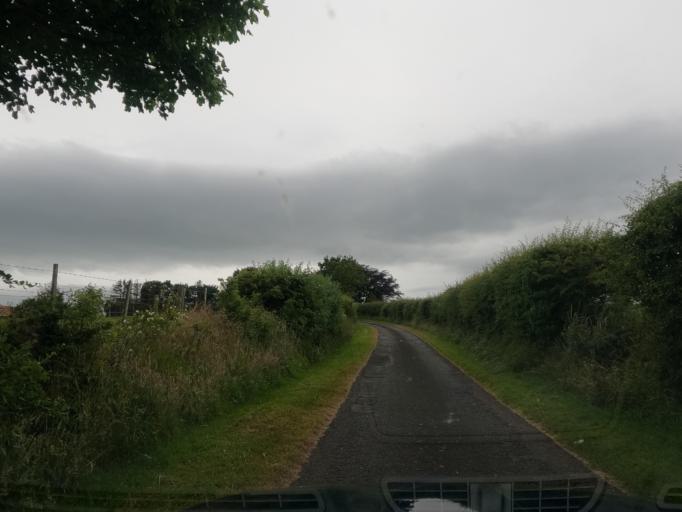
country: GB
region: England
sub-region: Northumberland
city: Lowick
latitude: 55.6527
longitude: -1.9077
